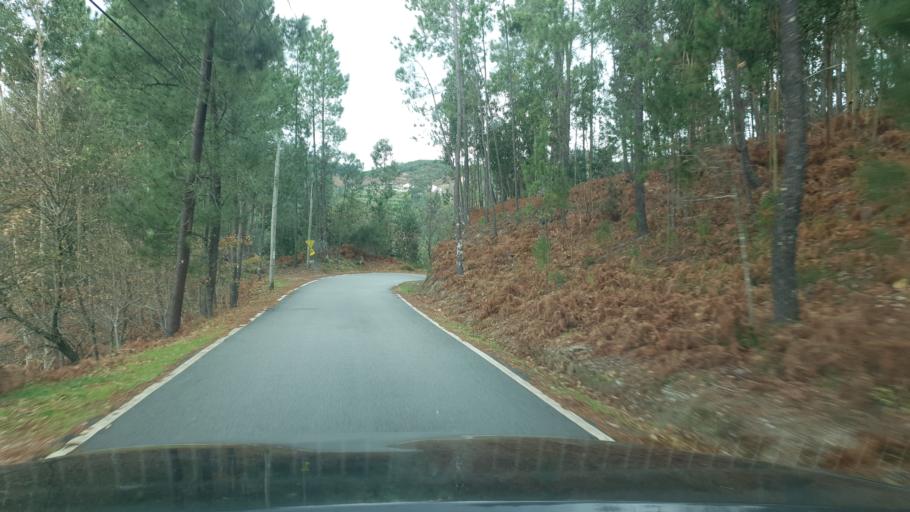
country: PT
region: Viseu
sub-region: Castro Daire
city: Castro Daire
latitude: 40.8828
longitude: -8.0132
